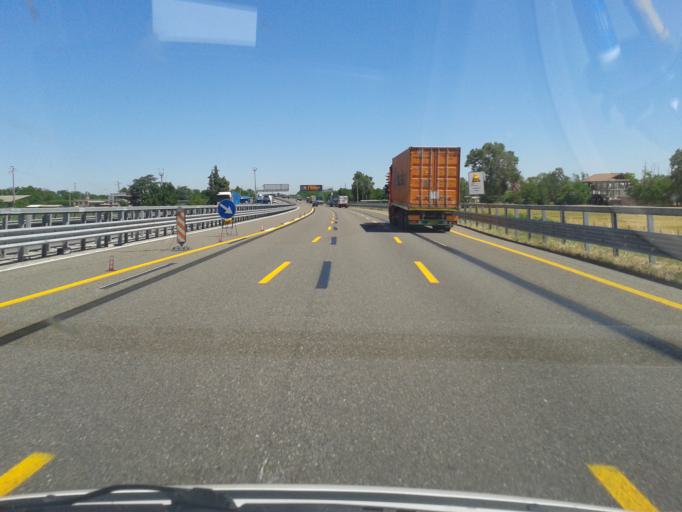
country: IT
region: Piedmont
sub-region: Provincia di Alessandria
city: Tortona
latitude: 44.8878
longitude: 8.8401
